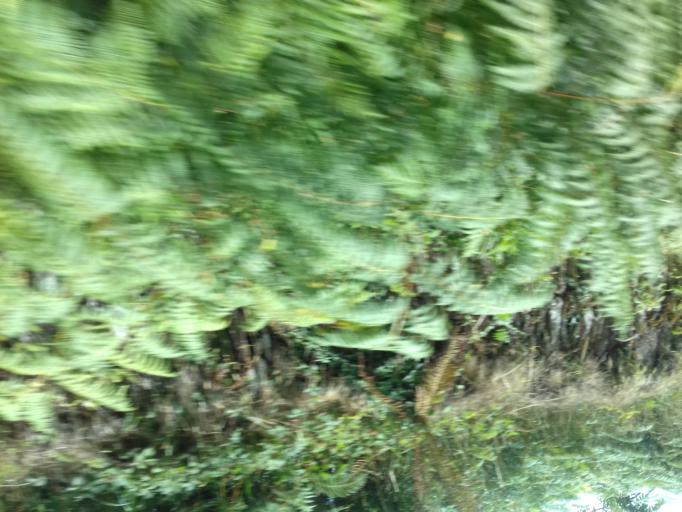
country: IE
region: Leinster
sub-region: Kilkenny
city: Graiguenamanagh
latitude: 52.6260
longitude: -6.8235
